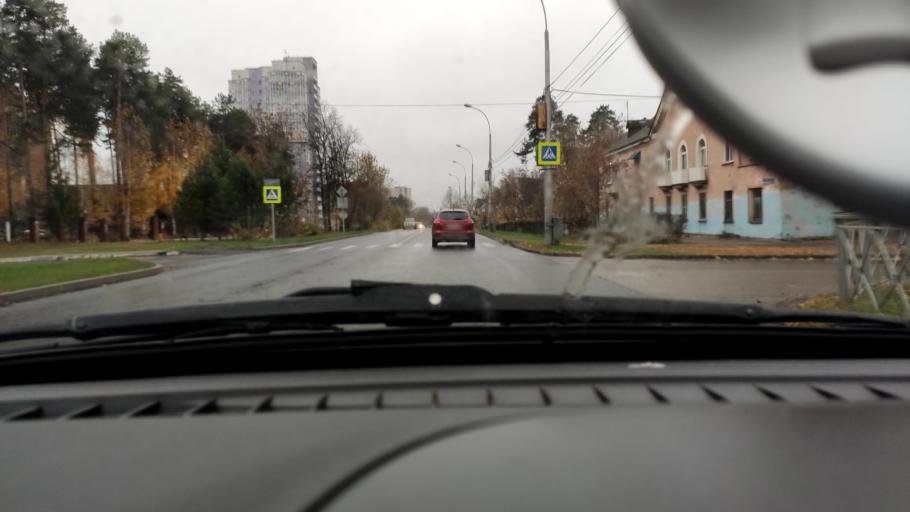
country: RU
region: Perm
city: Kultayevo
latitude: 58.0016
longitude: 55.9592
